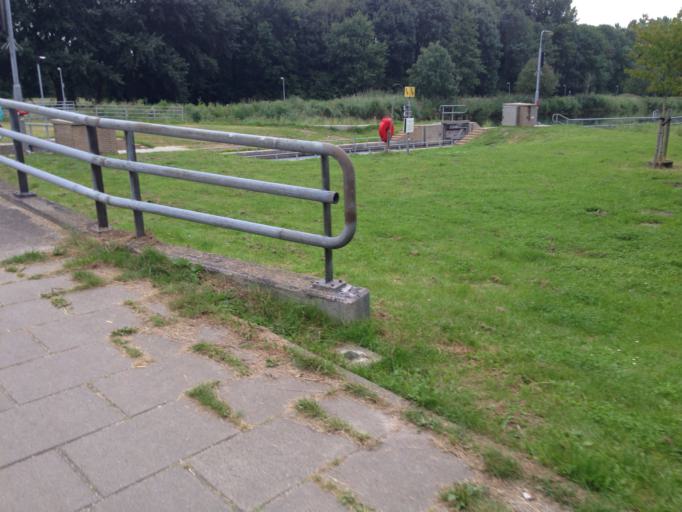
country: NL
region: Flevoland
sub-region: Gemeente Almere
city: Almere Stad
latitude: 52.3852
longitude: 5.2387
